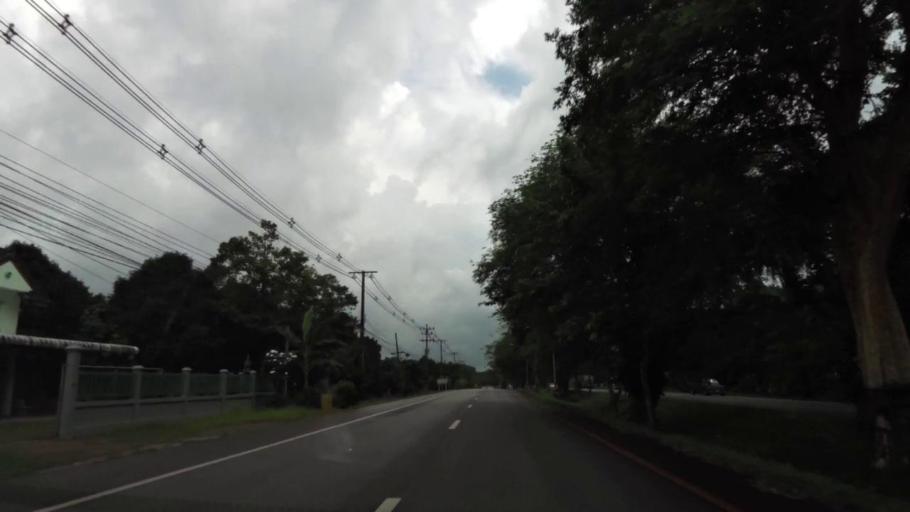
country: TH
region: Chanthaburi
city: Chanthaburi
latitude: 12.5658
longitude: 102.1613
